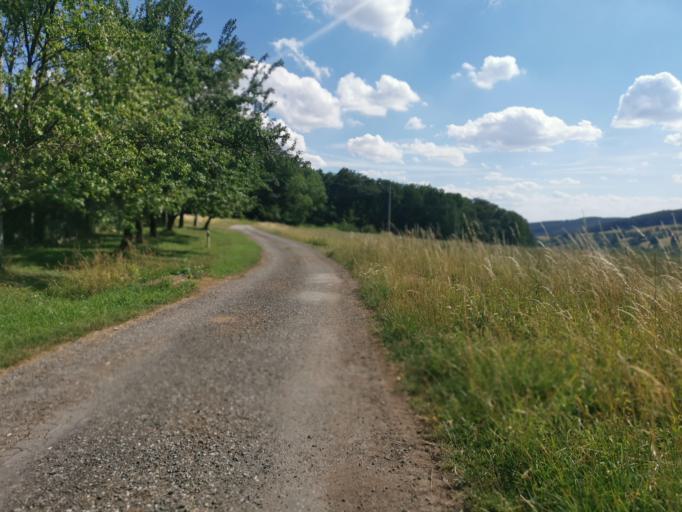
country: CZ
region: South Moravian
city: Knezdub
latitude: 48.8185
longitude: 17.4182
